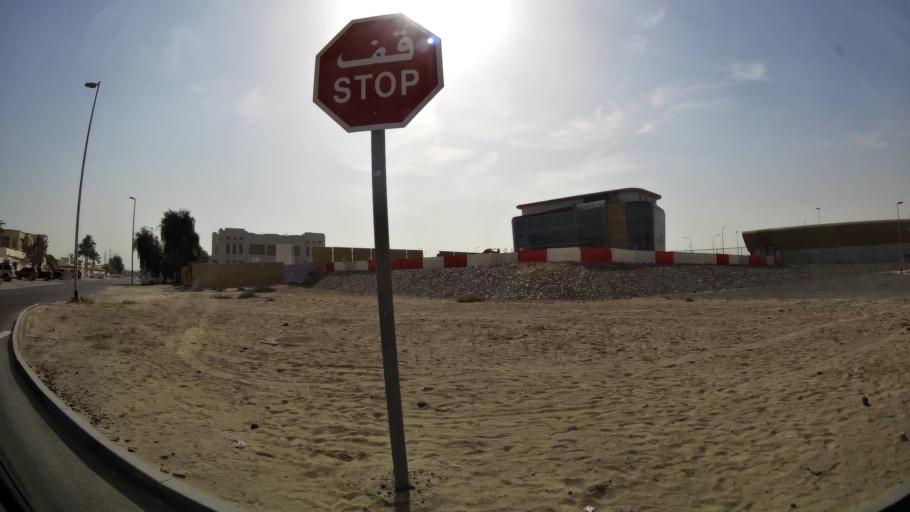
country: AE
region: Ash Shariqah
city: Sharjah
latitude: 25.2583
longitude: 55.4031
